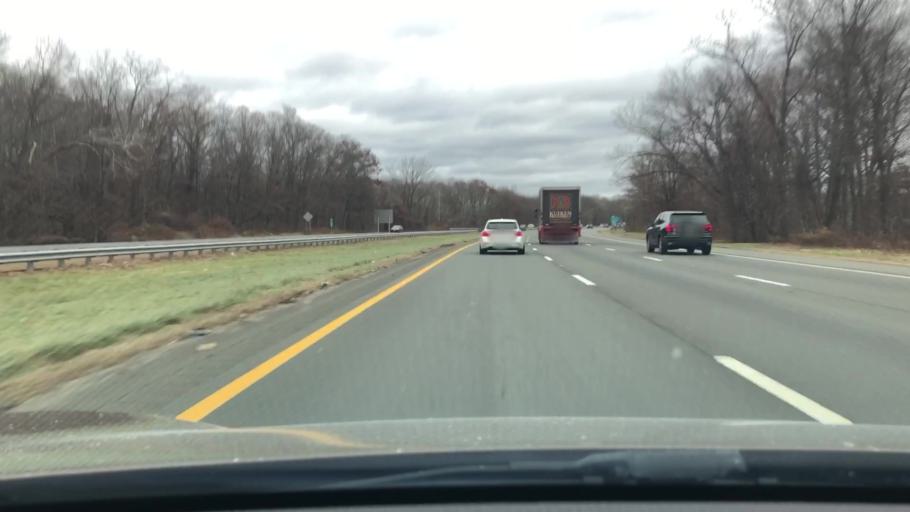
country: US
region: New Jersey
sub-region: Morris County
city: Wharton
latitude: 40.9084
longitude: -74.5967
